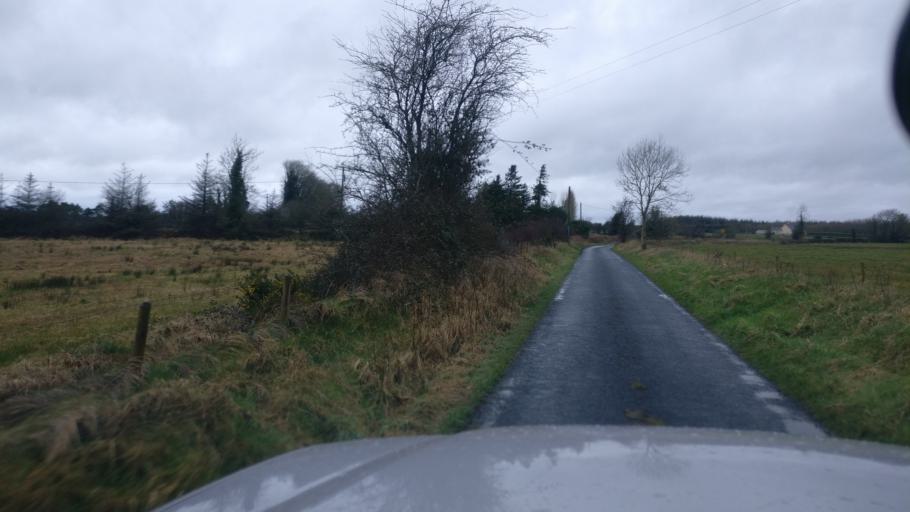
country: IE
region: Connaught
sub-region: County Galway
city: Ballinasloe
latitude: 53.2522
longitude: -8.3498
